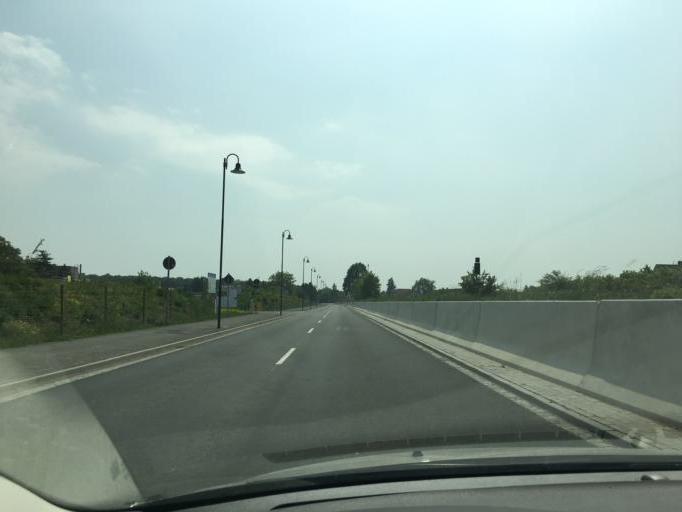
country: DE
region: Saxony
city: Naunhof
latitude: 51.2842
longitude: 12.5910
